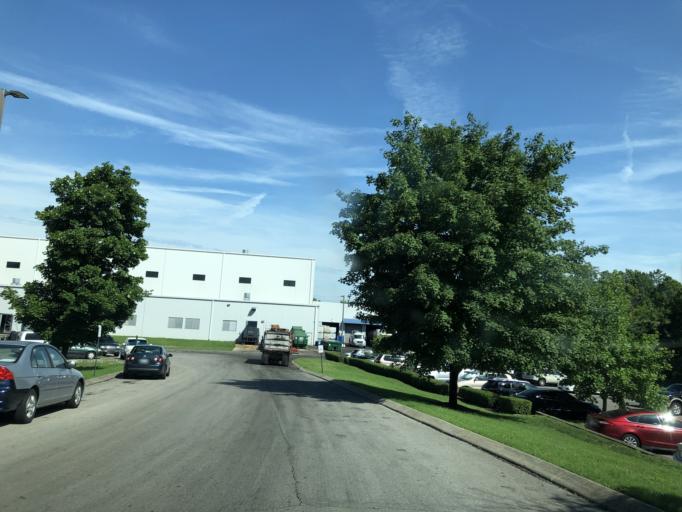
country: US
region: Tennessee
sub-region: Rutherford County
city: La Vergne
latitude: 36.0366
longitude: -86.6339
